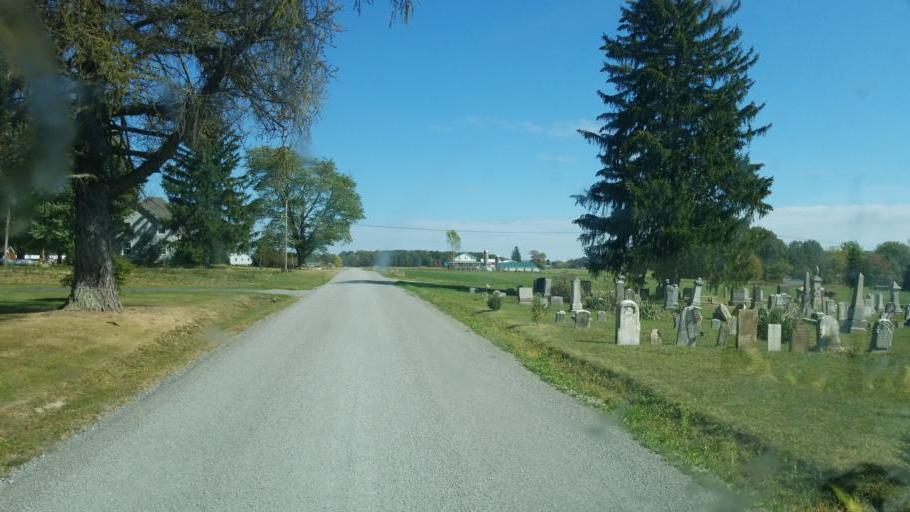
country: US
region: Pennsylvania
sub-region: Mercer County
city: Reynolds Heights
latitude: 41.3326
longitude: -80.3184
